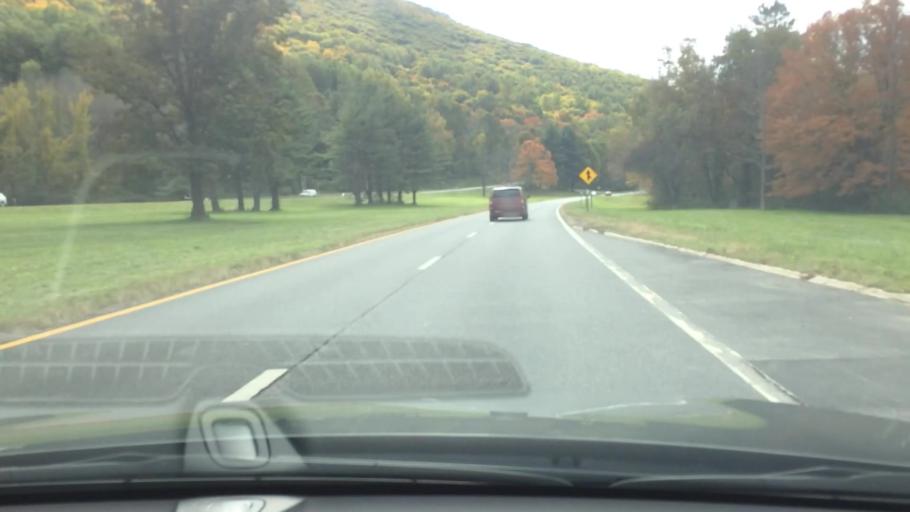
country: US
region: New York
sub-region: Dutchess County
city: Hillside Lake
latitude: 41.5373
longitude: -73.7717
